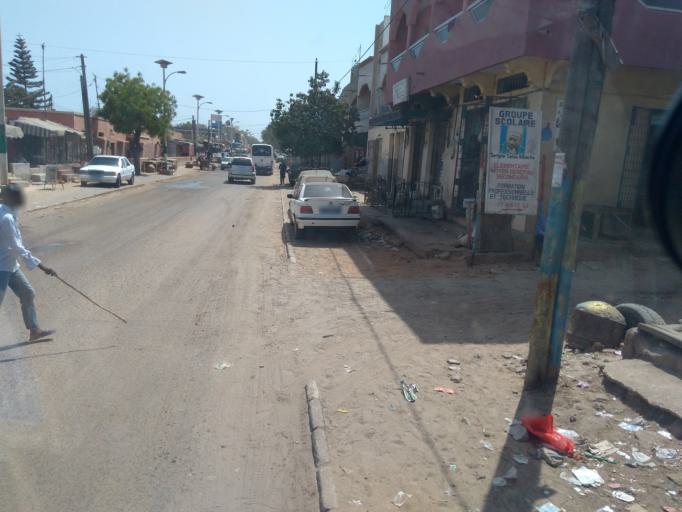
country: SN
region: Dakar
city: Pikine
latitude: 14.7644
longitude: -17.3727
